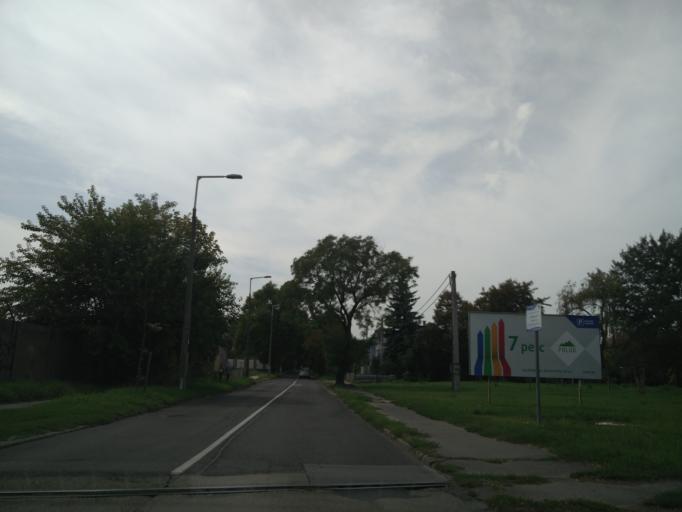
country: HU
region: Budapest
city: Budapest XV. keruelet
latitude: 47.5729
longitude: 19.1208
